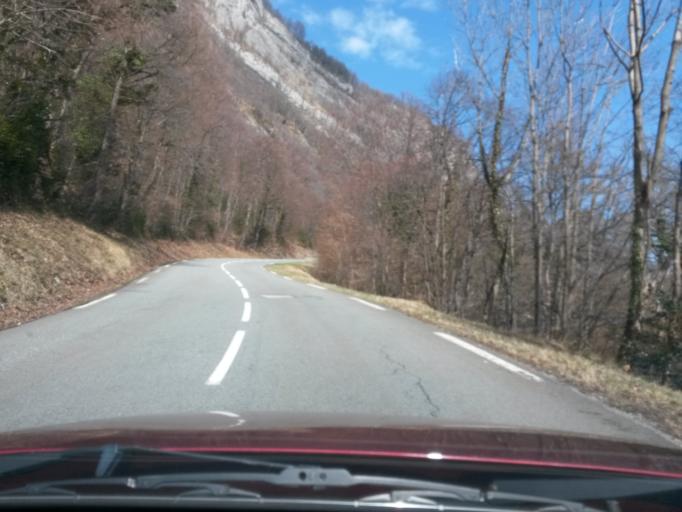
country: FR
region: Rhone-Alpes
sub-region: Departement de l'Isere
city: Bernin
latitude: 45.2756
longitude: 5.8387
